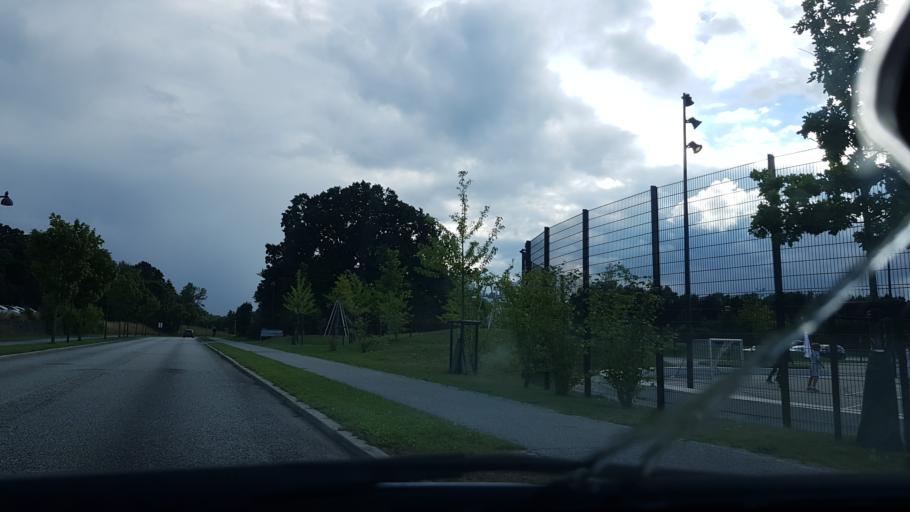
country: DK
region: Capital Region
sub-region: Fredensborg Kommune
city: Kokkedal
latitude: 55.9086
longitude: 12.4897
